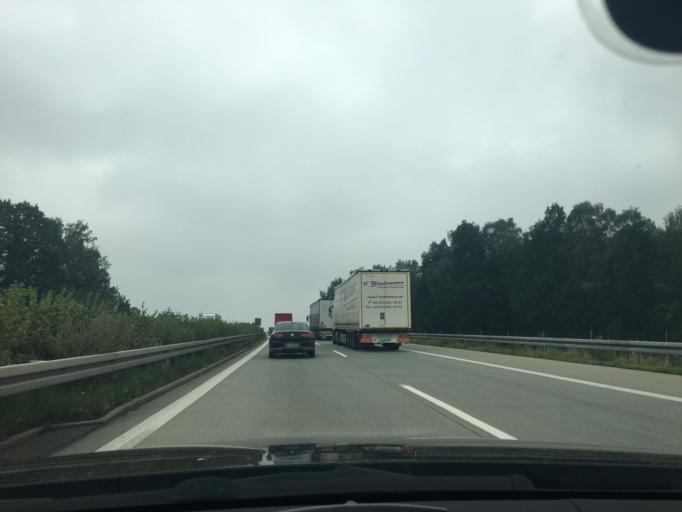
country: DE
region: Saxony
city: Neukirchen
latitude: 50.7861
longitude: 12.8302
